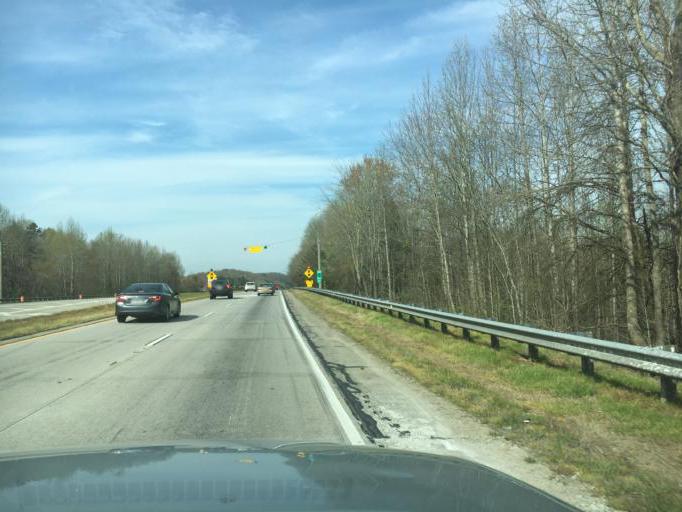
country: US
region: Georgia
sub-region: Hall County
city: Gainesville
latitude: 34.3279
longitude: -83.7849
